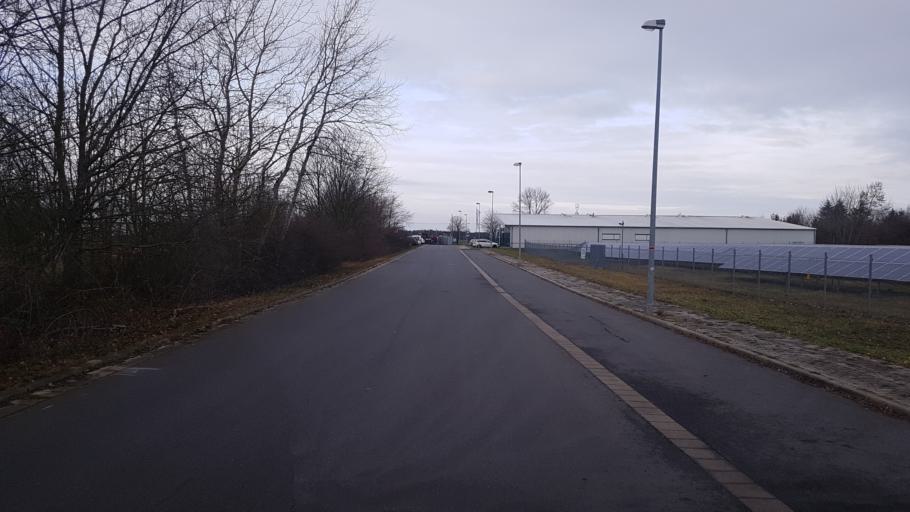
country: DE
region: Brandenburg
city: Sonnewalde
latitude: 51.6766
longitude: 13.6469
